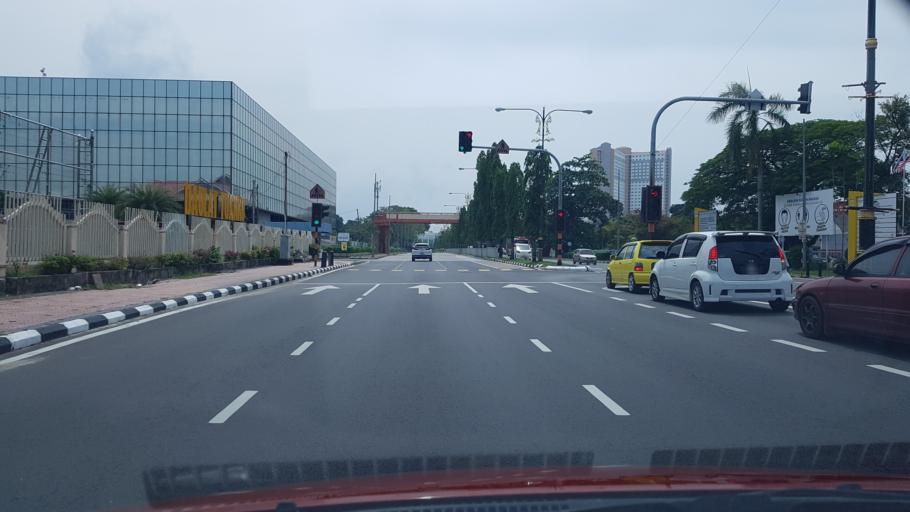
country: MY
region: Terengganu
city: Kuala Terengganu
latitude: 5.3234
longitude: 103.1507
